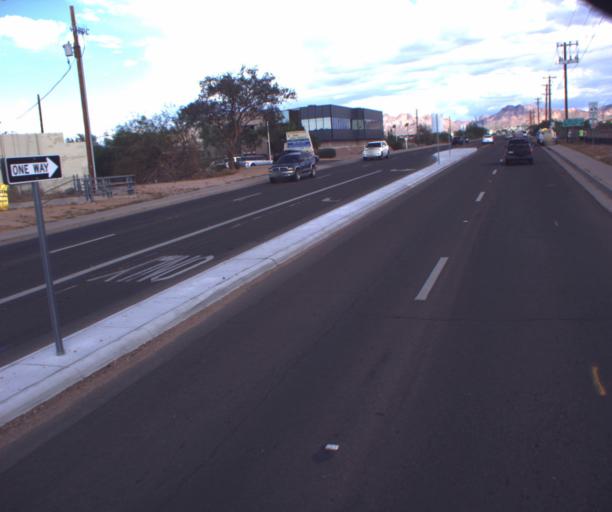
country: US
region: Arizona
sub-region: Pinal County
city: Apache Junction
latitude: 33.4135
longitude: -111.5460
